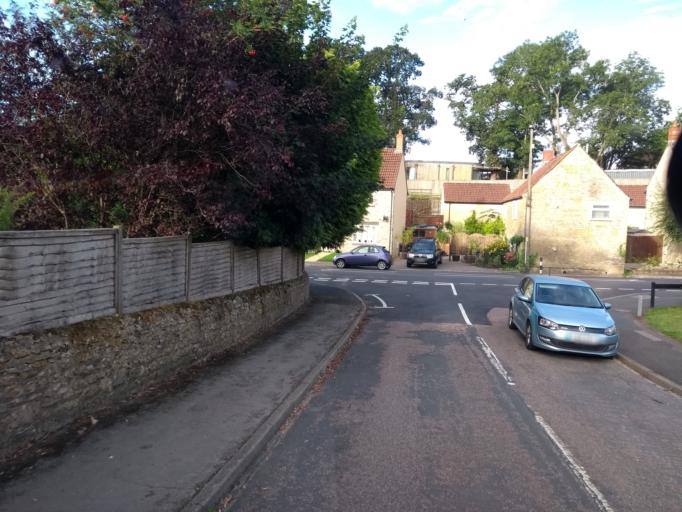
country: GB
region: England
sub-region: Dorset
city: Beaminster
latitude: 50.8109
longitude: -2.7431
